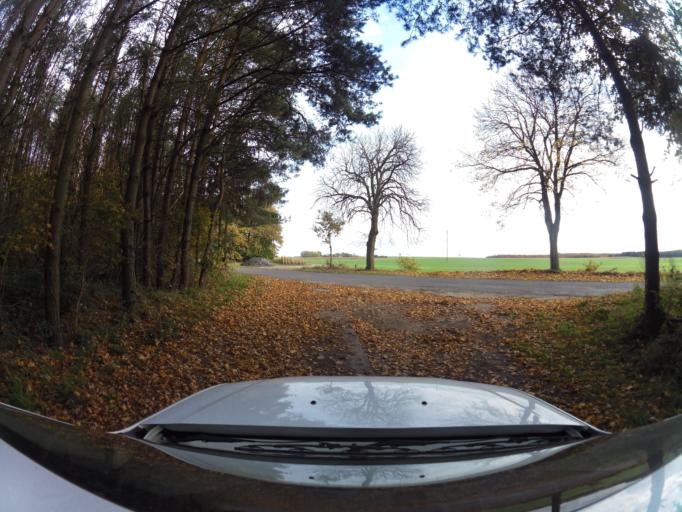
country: PL
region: West Pomeranian Voivodeship
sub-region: Powiat gryficki
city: Gryfice
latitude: 53.8712
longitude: 15.1214
